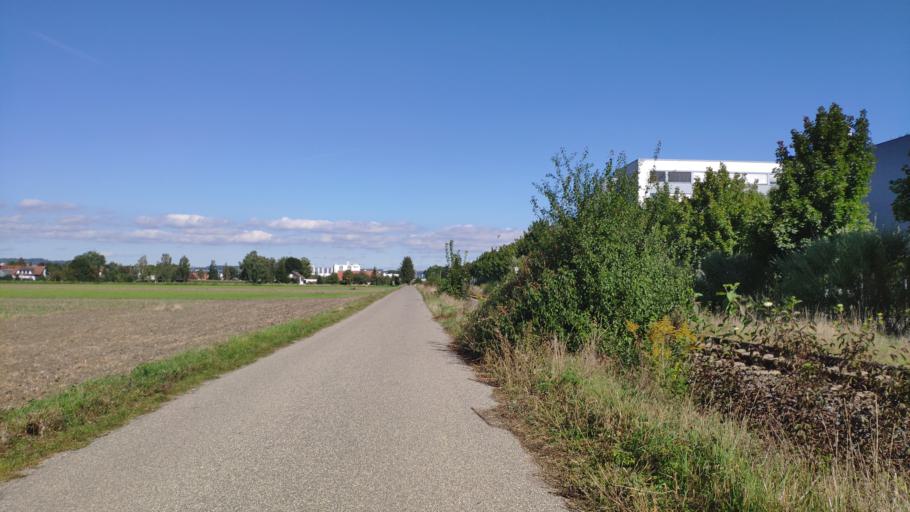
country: DE
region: Bavaria
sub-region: Swabia
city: Neu-Ulm
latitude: 48.3751
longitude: 10.0303
